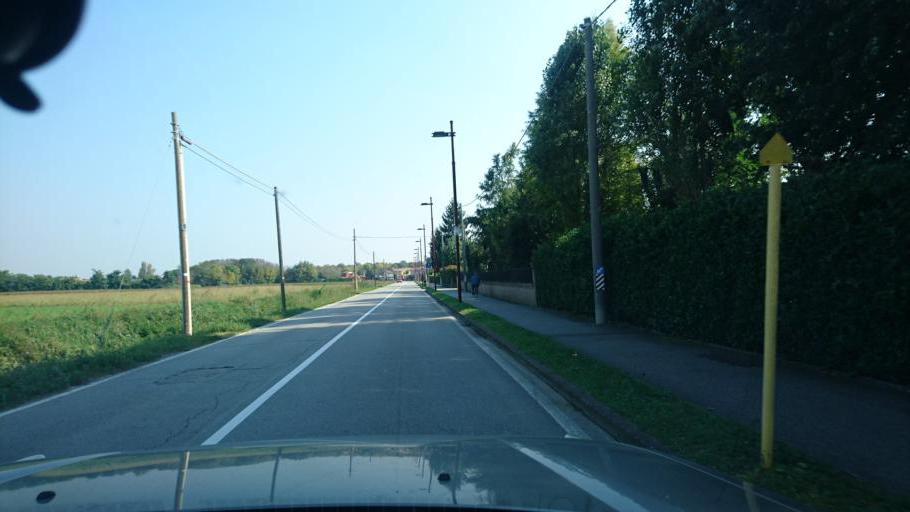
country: IT
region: Veneto
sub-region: Provincia di Padova
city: Bosco
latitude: 45.4410
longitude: 11.8034
